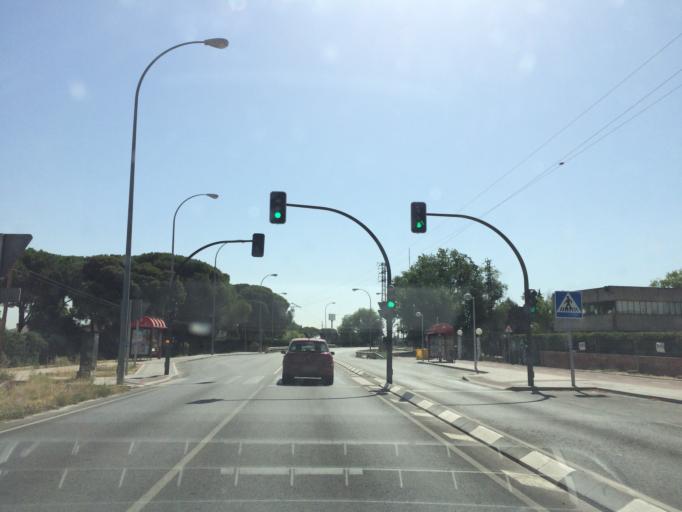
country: ES
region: Madrid
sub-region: Provincia de Madrid
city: Pozuelo de Alarcon
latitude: 40.4395
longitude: -3.8390
